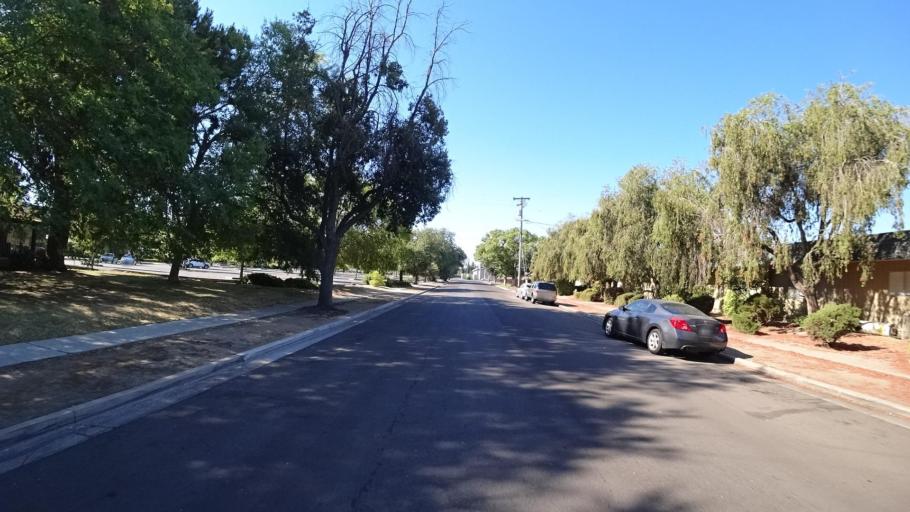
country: US
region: California
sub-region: Fresno County
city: Fresno
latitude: 36.7883
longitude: -119.7568
